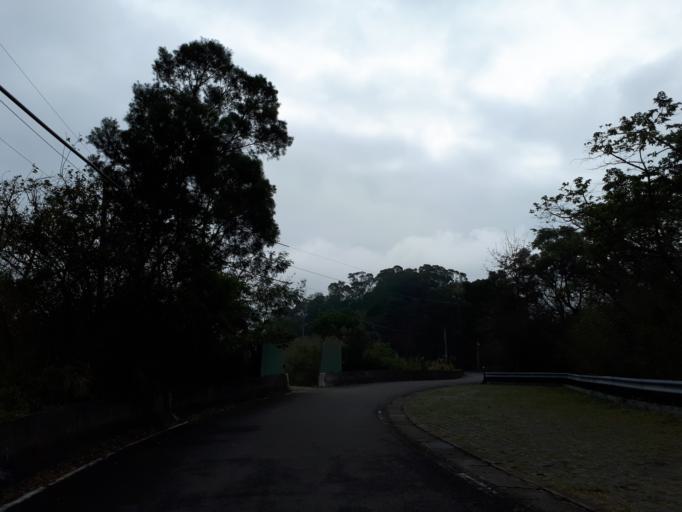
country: TW
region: Taiwan
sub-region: Hsinchu
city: Hsinchu
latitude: 24.7393
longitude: 121.0578
